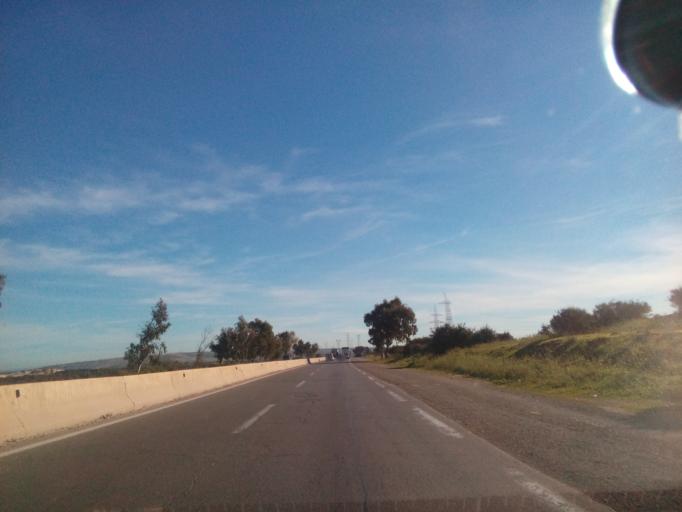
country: DZ
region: Oran
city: Ain el Bya
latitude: 35.7830
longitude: -0.1393
